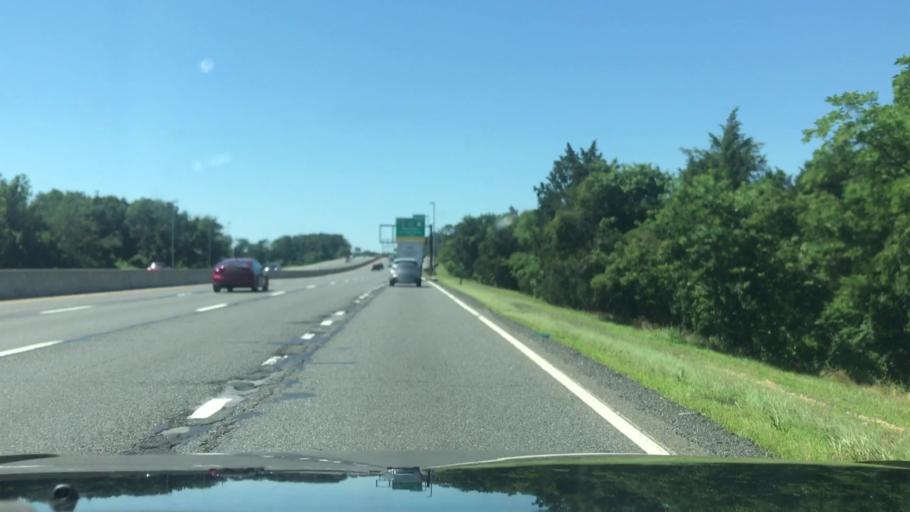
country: US
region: New Jersey
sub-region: Ocean County
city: South Toms River
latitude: 39.9463
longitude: -74.2083
